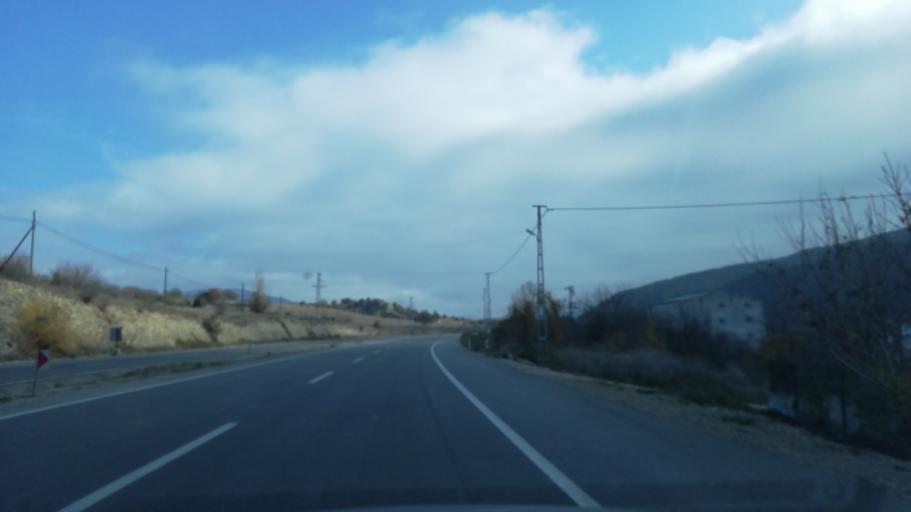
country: TR
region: Karabuk
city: Safranbolu
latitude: 41.2183
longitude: 32.7454
